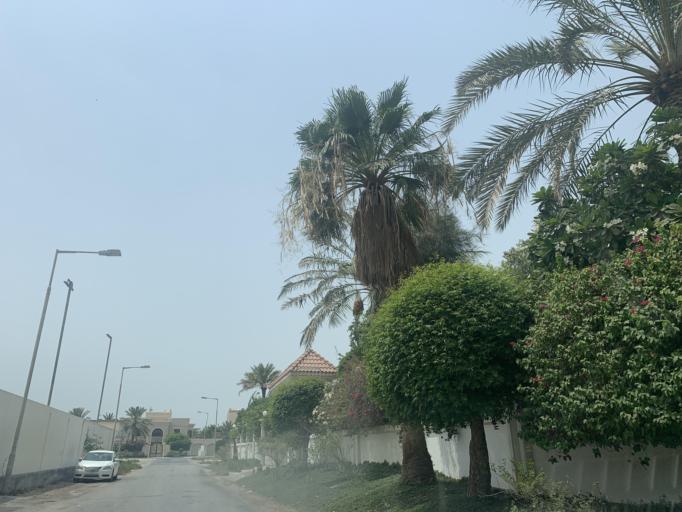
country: BH
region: Northern
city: Madinat `Isa
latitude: 26.1928
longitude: 50.4654
